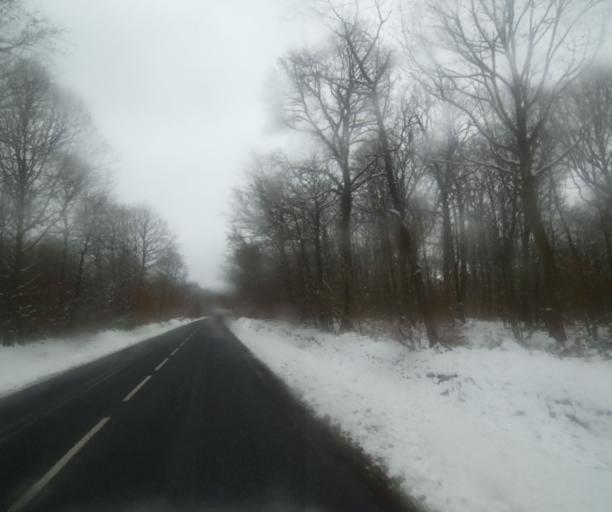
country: FR
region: Champagne-Ardenne
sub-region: Departement de la Haute-Marne
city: Laneuville-a-Remy
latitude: 48.4551
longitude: 4.8773
